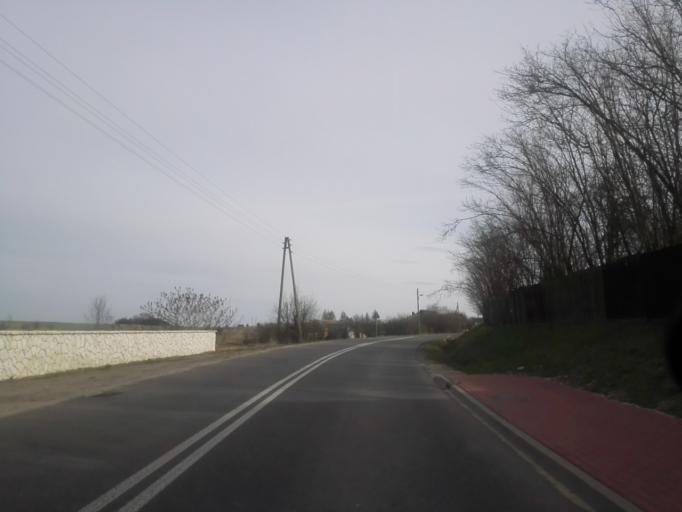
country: PL
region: Silesian Voivodeship
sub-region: Powiat czestochowski
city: Olsztyn
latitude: 50.7188
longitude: 19.3335
